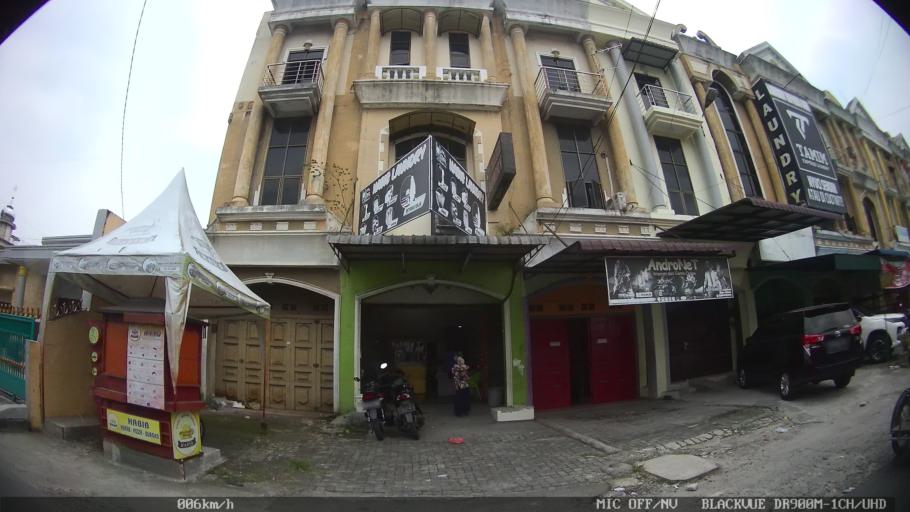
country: ID
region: North Sumatra
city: Medan
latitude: 3.5661
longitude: 98.7024
